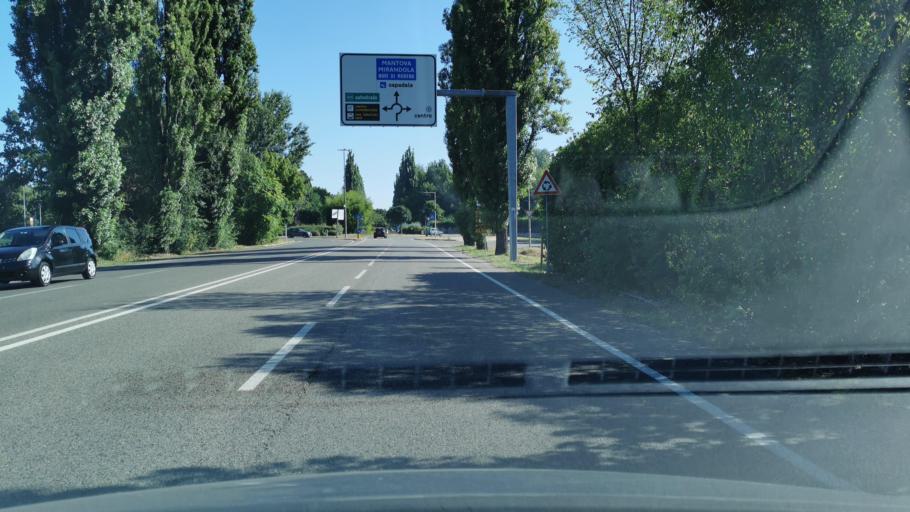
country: IT
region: Emilia-Romagna
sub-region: Provincia di Modena
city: Carpi Centro
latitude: 44.7798
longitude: 10.8663
